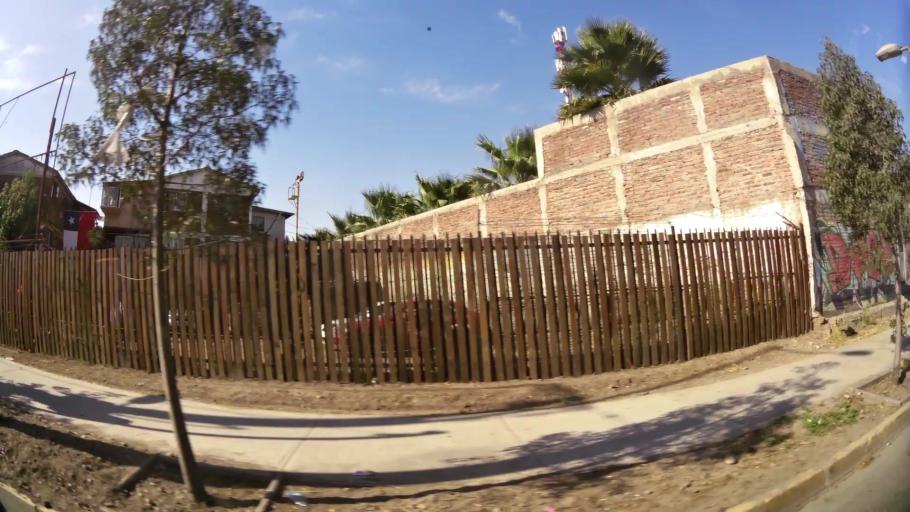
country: CL
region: Santiago Metropolitan
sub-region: Provincia de Santiago
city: Santiago
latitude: -33.4882
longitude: -70.6837
